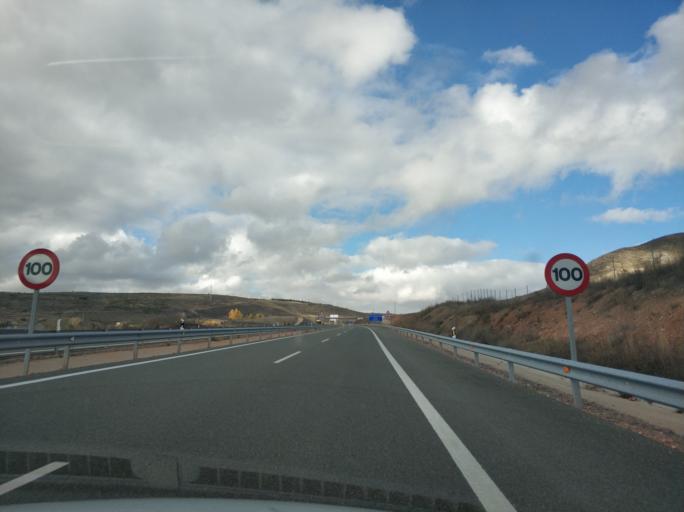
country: ES
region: Castille and Leon
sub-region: Provincia de Soria
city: Medinaceli
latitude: 41.1788
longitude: -2.4264
